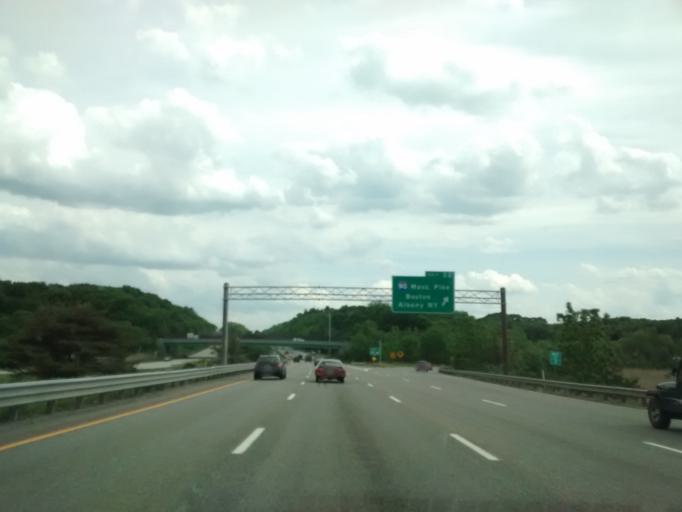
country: US
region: Massachusetts
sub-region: Worcester County
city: Cordaville
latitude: 42.2653
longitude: -71.5643
